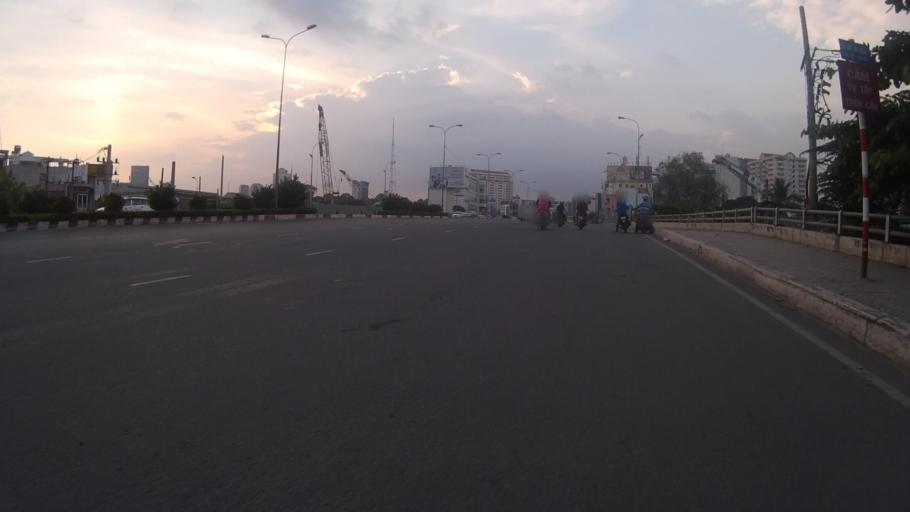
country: VN
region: Ho Chi Minh City
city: Quan Mot
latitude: 10.7896
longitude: 106.7138
